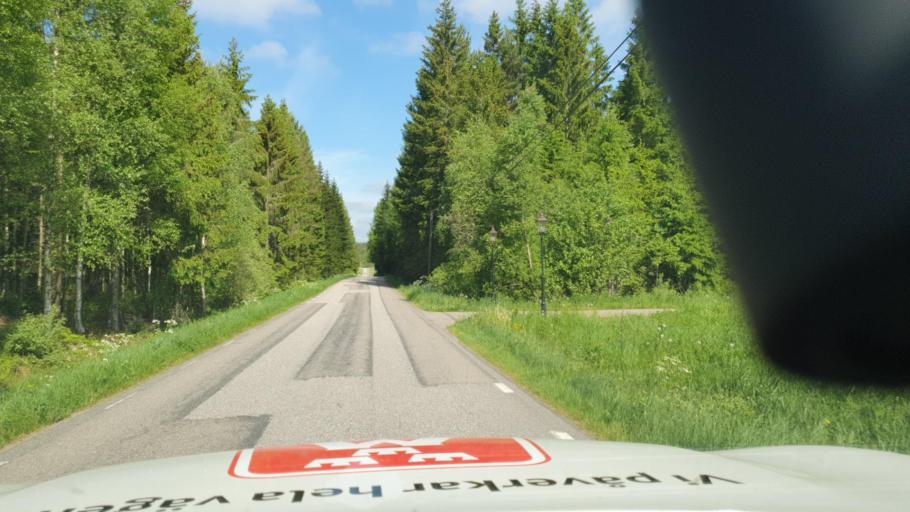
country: SE
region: Vaestra Goetaland
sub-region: Herrljunga Kommun
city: Herrljunga
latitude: 57.9326
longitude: 13.0339
